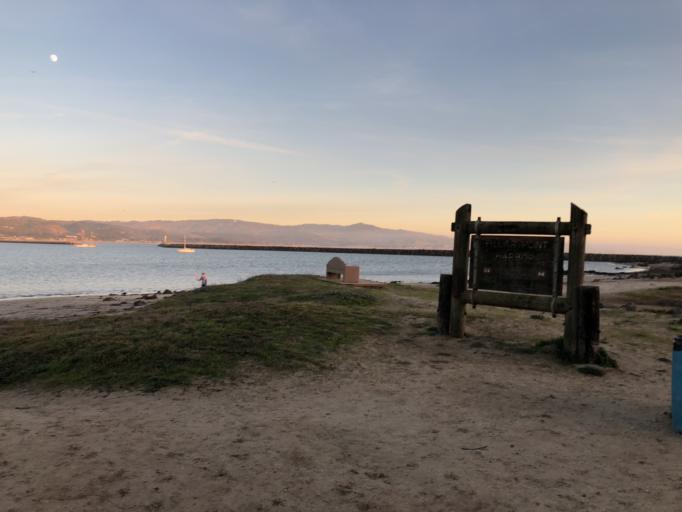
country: US
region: California
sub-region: San Mateo County
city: El Granada
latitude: 37.4960
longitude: -122.4951
